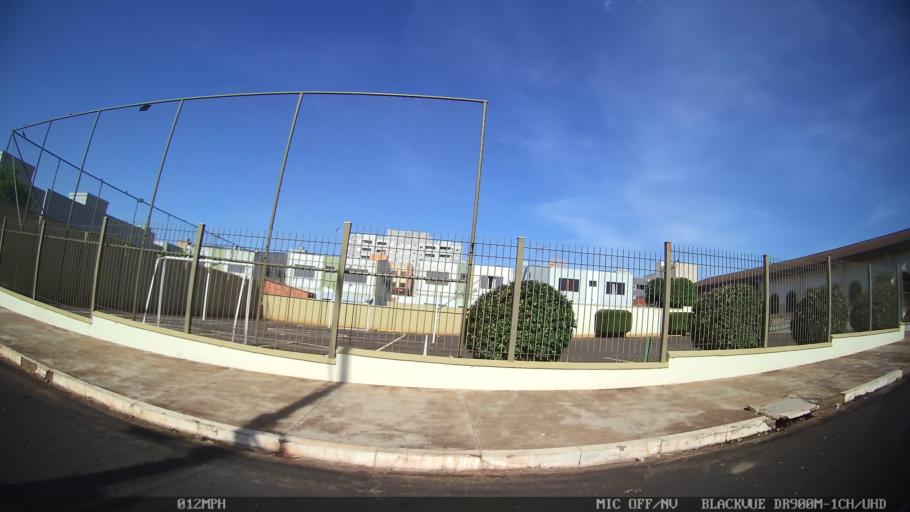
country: BR
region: Sao Paulo
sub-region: Ribeirao Preto
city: Ribeirao Preto
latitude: -21.1753
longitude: -47.7603
